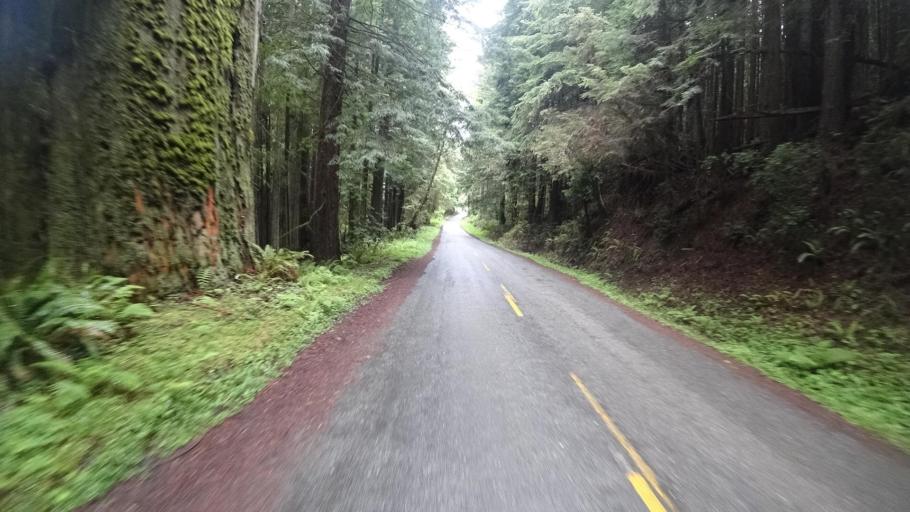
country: US
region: California
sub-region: Humboldt County
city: Bayside
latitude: 40.8213
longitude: -124.0314
